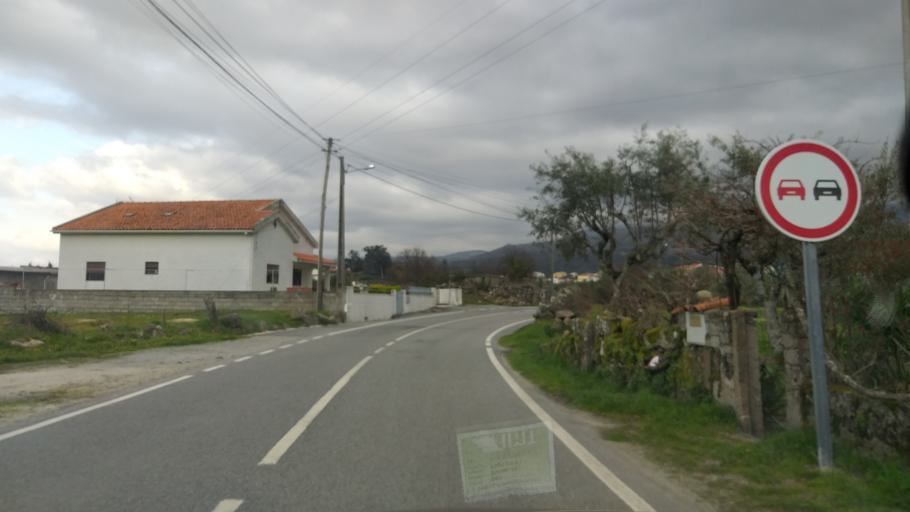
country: PT
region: Guarda
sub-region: Seia
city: Seia
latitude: 40.4743
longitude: -7.6390
